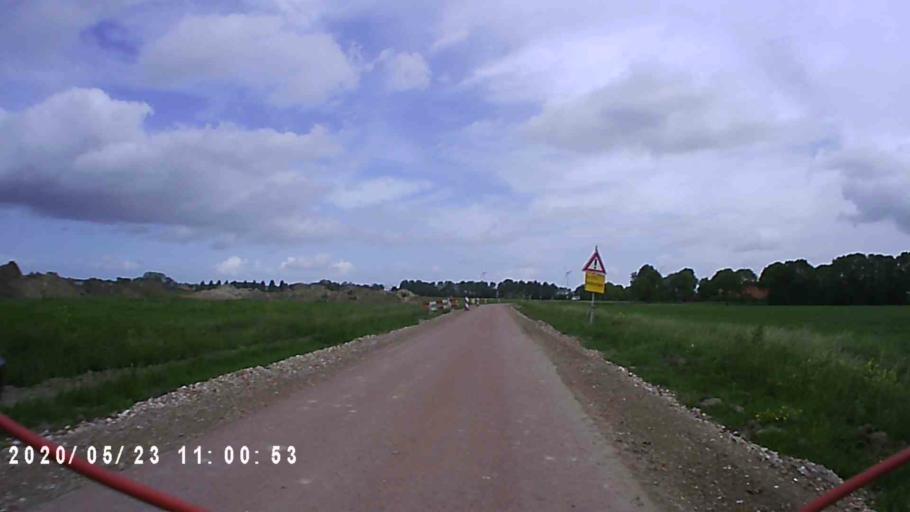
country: NL
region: Groningen
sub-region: Gemeente Delfzijl
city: Delfzijl
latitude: 53.3072
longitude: 6.9433
